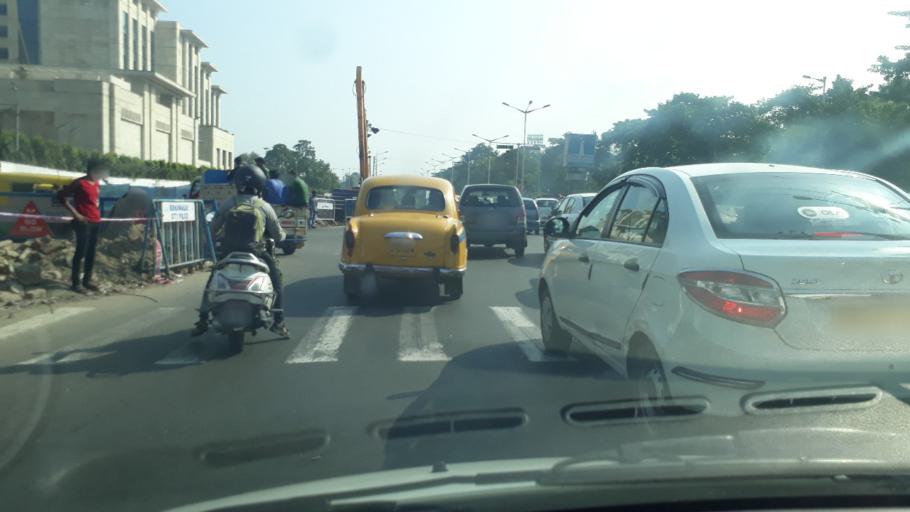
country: IN
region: West Bengal
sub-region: Kolkata
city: Kolkata
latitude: 22.5714
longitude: 88.4039
